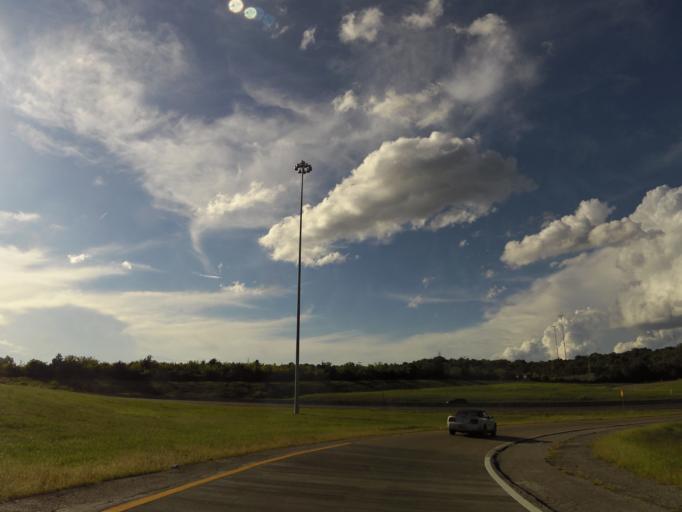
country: US
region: Tennessee
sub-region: Davidson County
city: Nashville
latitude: 36.2366
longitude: -86.7875
